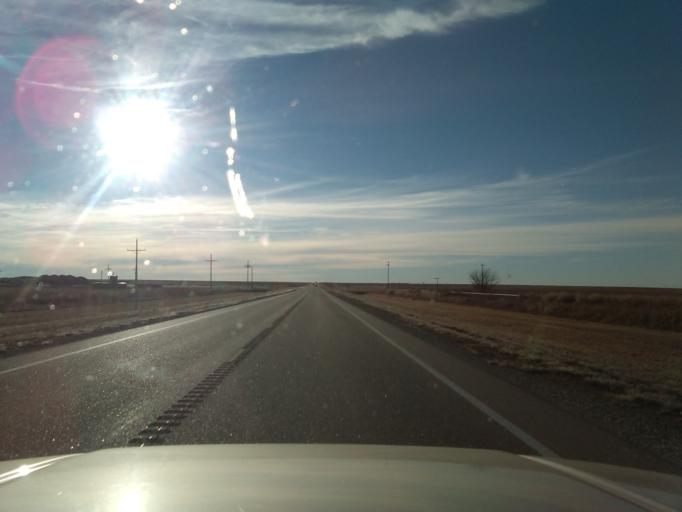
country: US
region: Kansas
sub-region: Sheridan County
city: Hoxie
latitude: 39.5354
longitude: -100.5881
